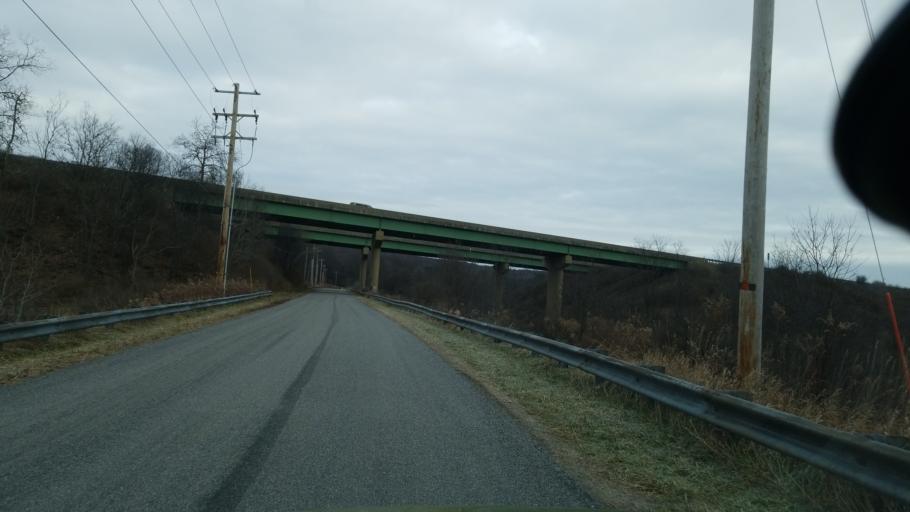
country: US
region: Pennsylvania
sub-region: Clearfield County
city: Treasure Lake
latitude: 41.1206
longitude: -78.6175
